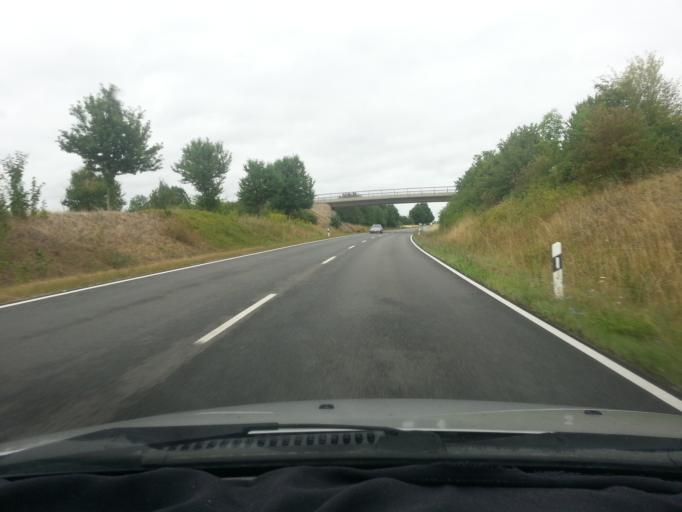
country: DE
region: Rheinland-Pfalz
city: Ruppertsberg
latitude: 49.3976
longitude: 8.2111
